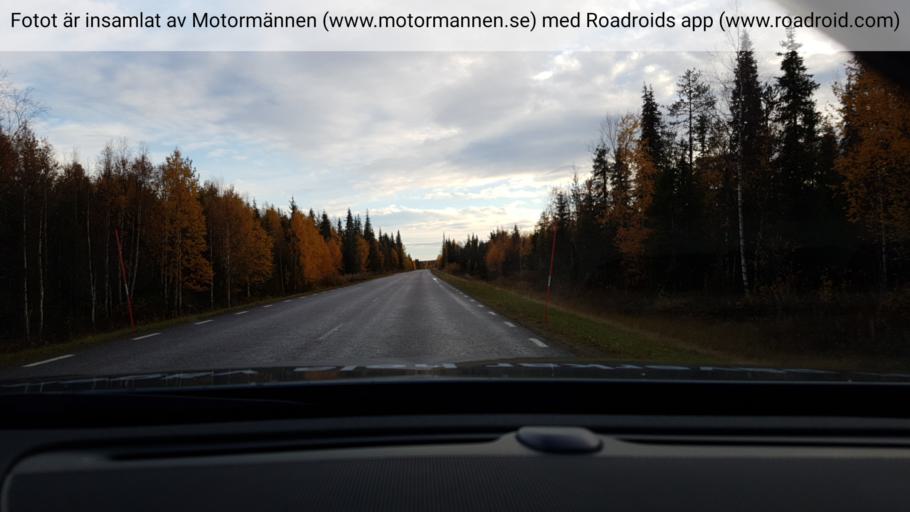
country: SE
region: Norrbotten
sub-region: Overkalix Kommun
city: OEverkalix
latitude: 66.9045
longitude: 22.7758
